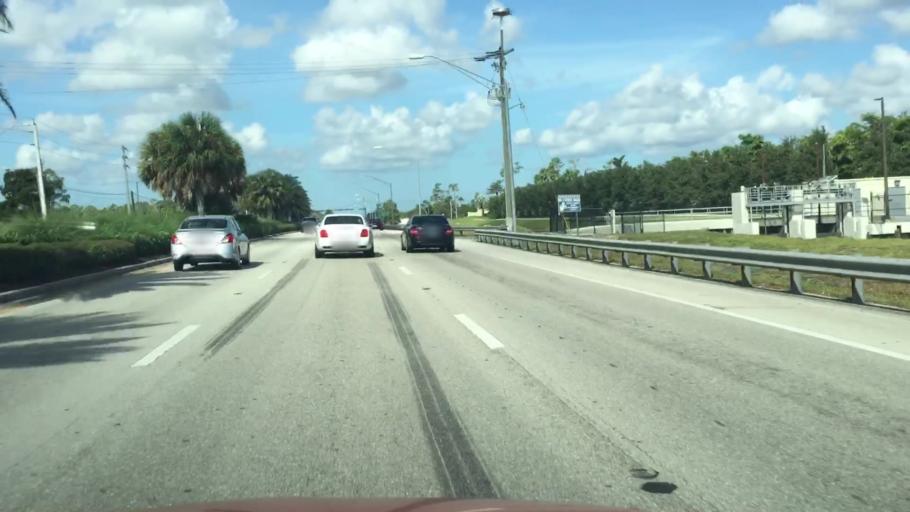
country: US
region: Florida
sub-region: Collier County
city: Vineyards
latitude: 26.2730
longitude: -81.7166
